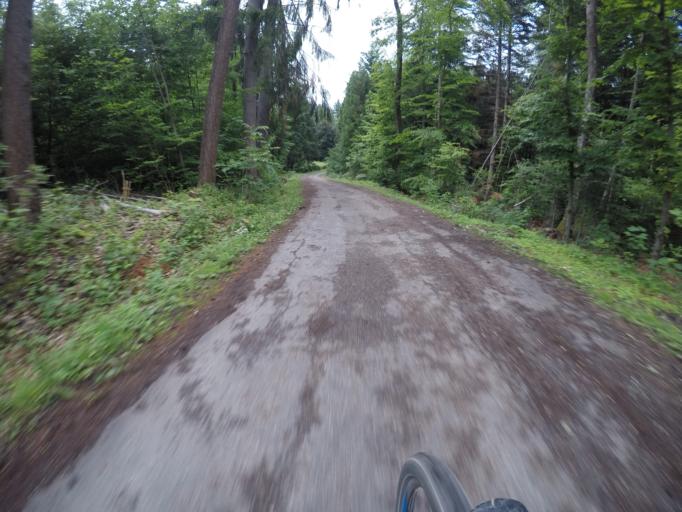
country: DE
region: Baden-Wuerttemberg
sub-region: Regierungsbezirk Stuttgart
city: Kohlberg
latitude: 48.5568
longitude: 9.3138
